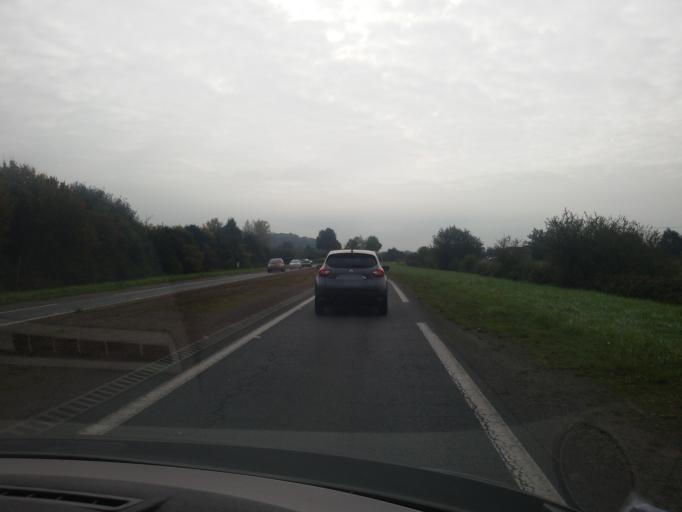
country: FR
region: Lower Normandy
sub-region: Departement du Calvados
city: Dives-sur-Mer
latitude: 49.2597
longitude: -0.1042
